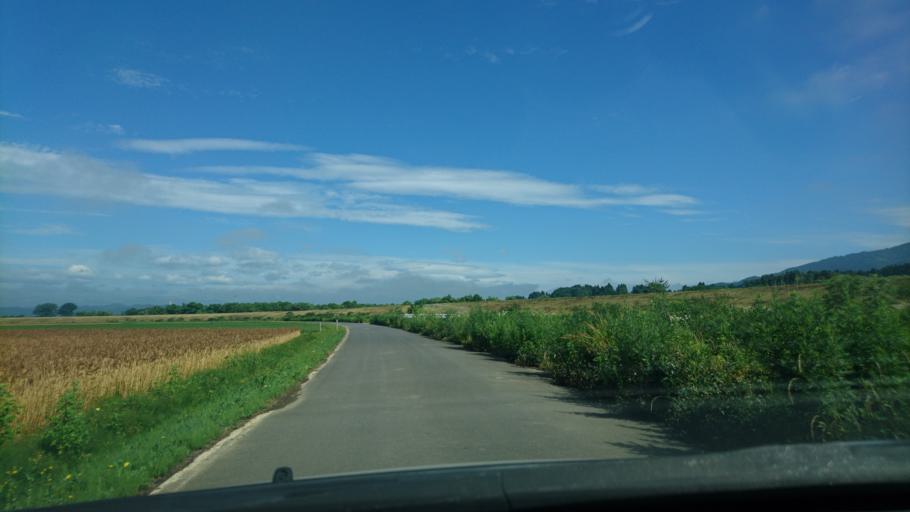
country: JP
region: Iwate
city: Ichinoseki
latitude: 38.9728
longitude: 141.1546
